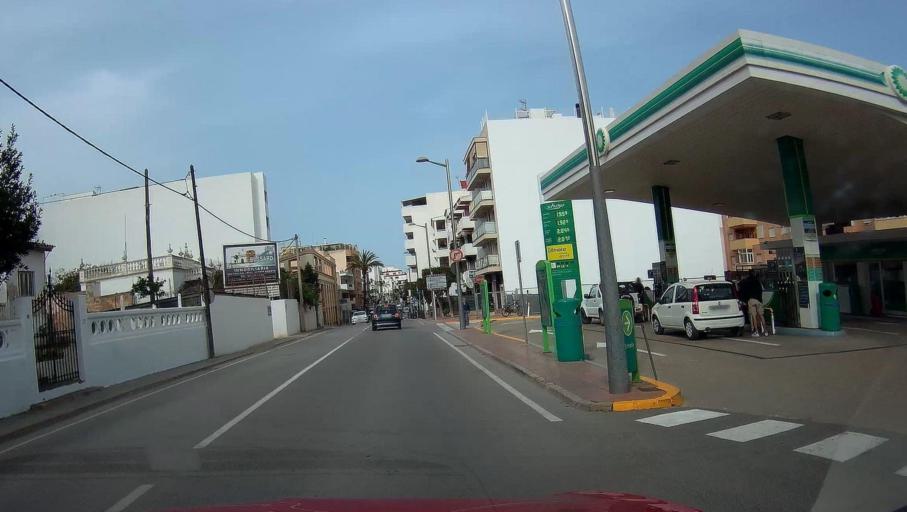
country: ES
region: Balearic Islands
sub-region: Illes Balears
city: Santa Eularia des Riu
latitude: 38.9836
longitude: 1.5317
